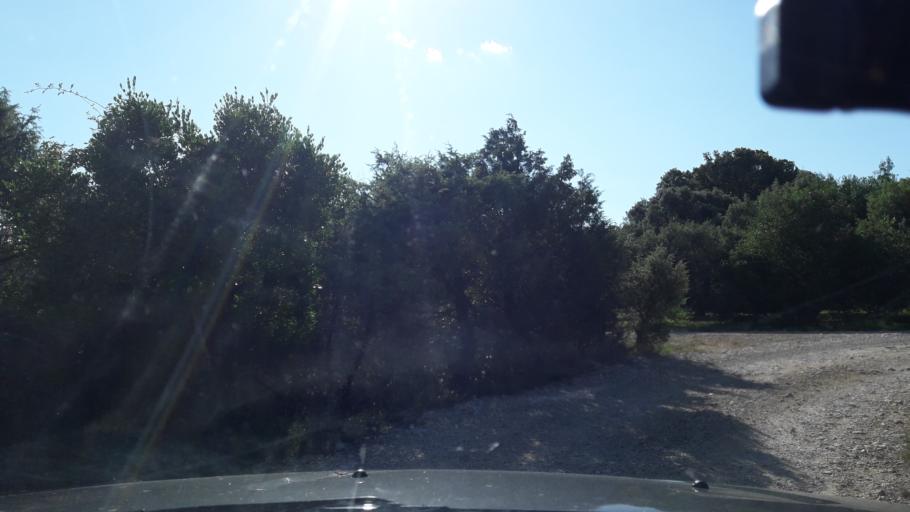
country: FR
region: Languedoc-Roussillon
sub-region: Departement du Gard
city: Saint-Julien-de-Peyrolas
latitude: 44.3654
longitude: 4.5246
